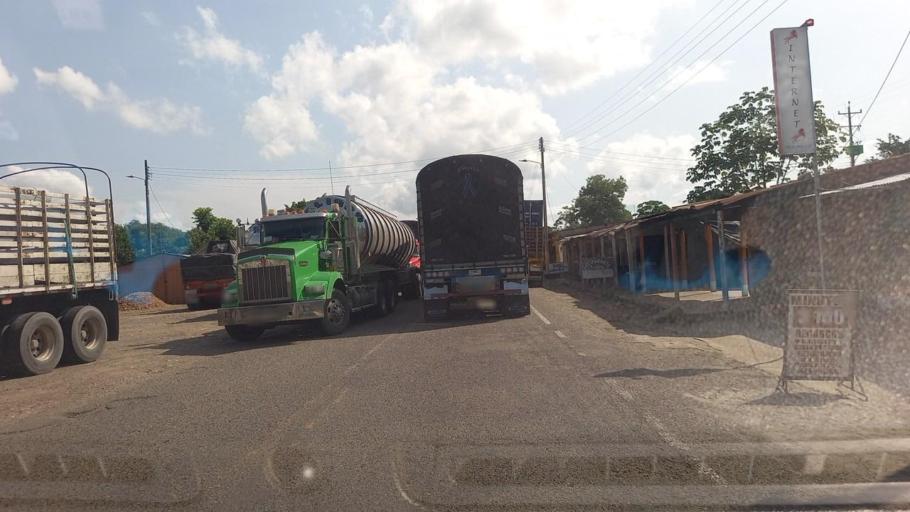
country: CO
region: Antioquia
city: Puerto Berrio
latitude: 6.3320
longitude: -74.4351
